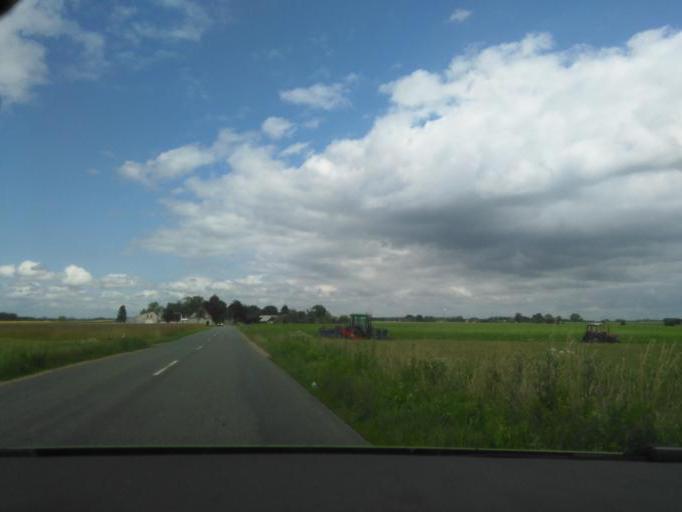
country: DK
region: Zealand
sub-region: Kalundborg Kommune
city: Gorlev
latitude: 55.5461
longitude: 11.1756
